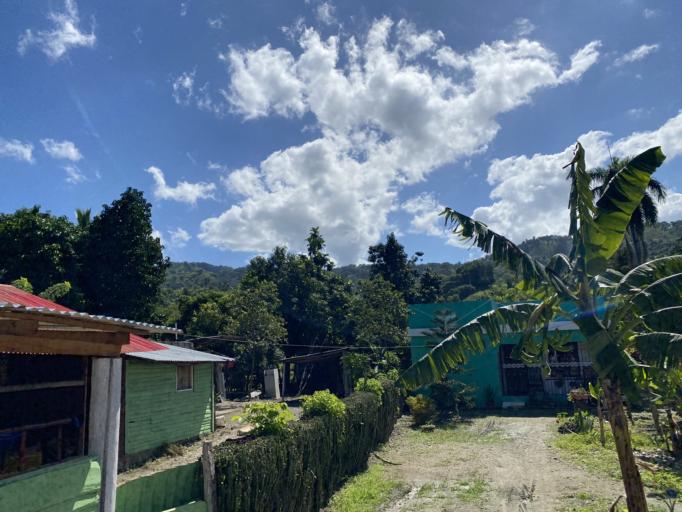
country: DO
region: Puerto Plata
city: Imbert
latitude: 19.7925
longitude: -70.8080
